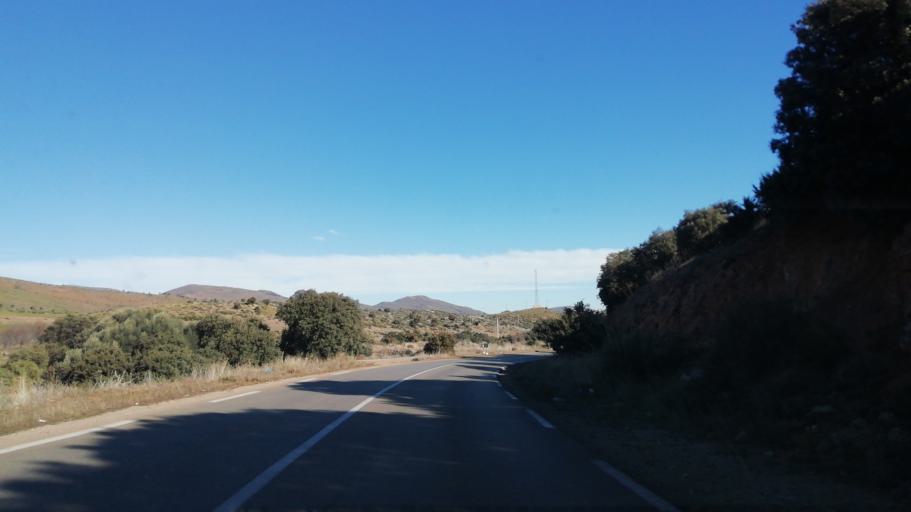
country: DZ
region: Tlemcen
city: Ouled Mimoun
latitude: 34.7610
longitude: -1.1446
